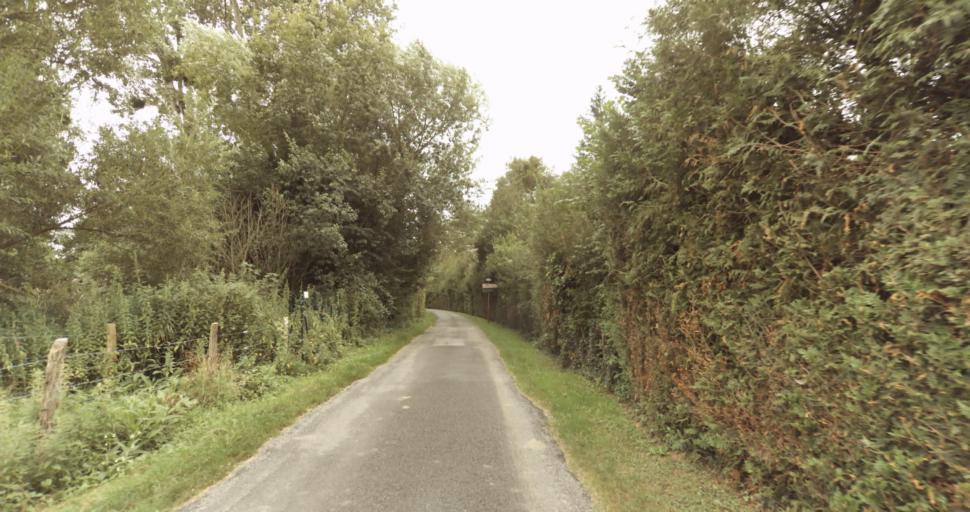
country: FR
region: Haute-Normandie
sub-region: Departement de l'Eure
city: Saint-Aubin-sur-Gaillon
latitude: 49.0817
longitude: 1.2842
